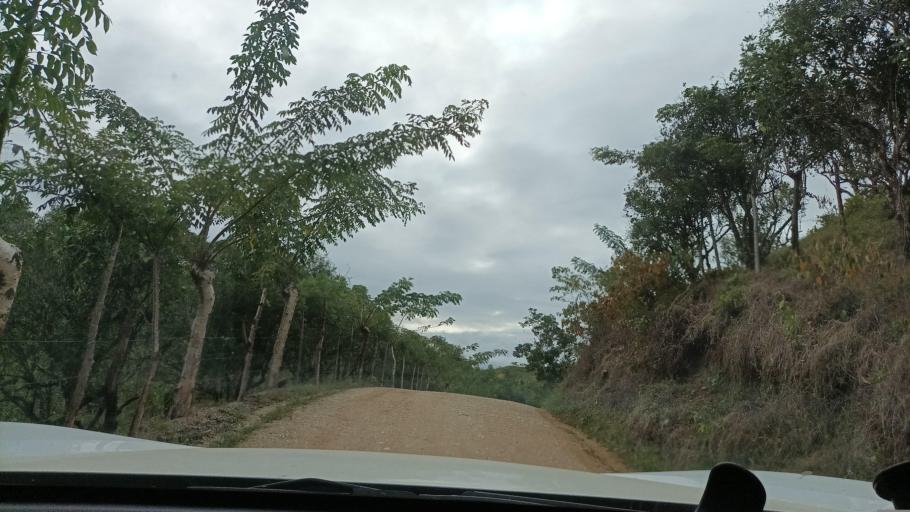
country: MX
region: Veracruz
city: Hidalgotitlan
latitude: 17.6029
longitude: -94.4242
